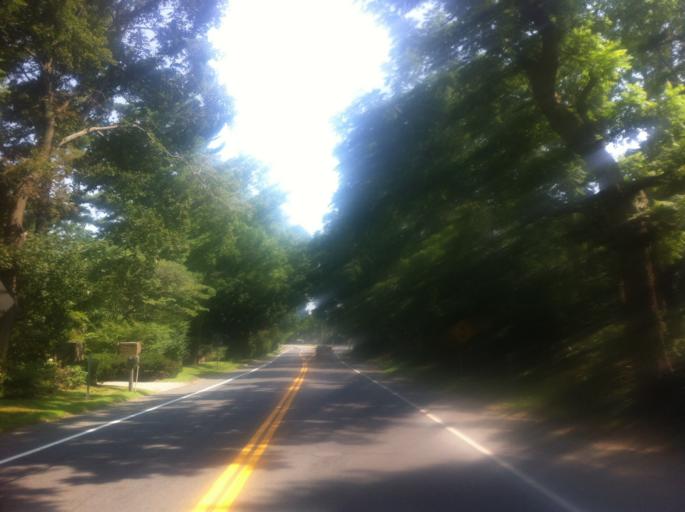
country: US
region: New York
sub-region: Nassau County
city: Brookville
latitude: 40.8046
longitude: -73.5537
